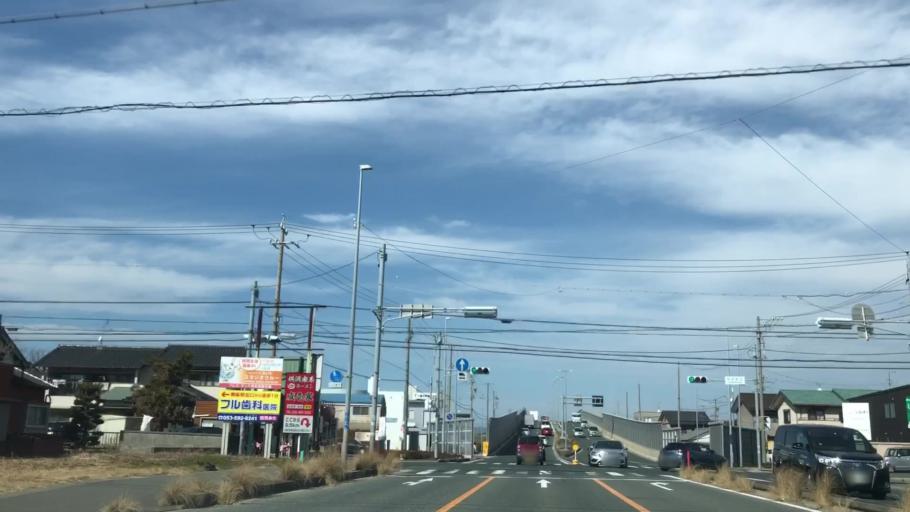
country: JP
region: Shizuoka
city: Hamamatsu
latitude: 34.6830
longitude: 137.6478
